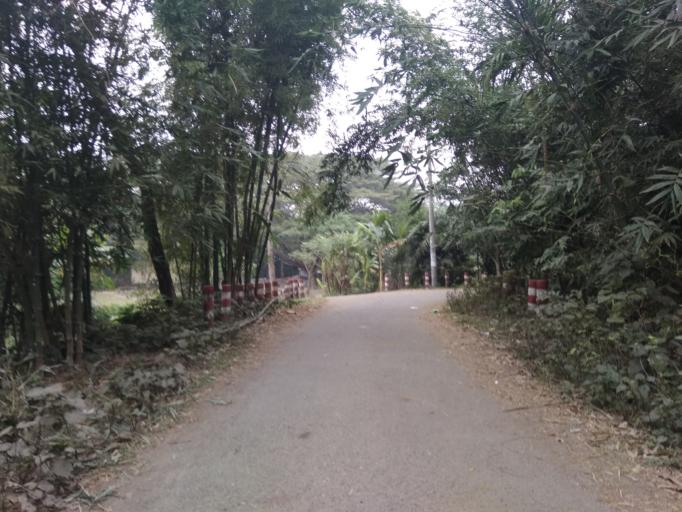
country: BD
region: Barisal
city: Mehendiganj
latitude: 22.9222
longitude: 90.3917
